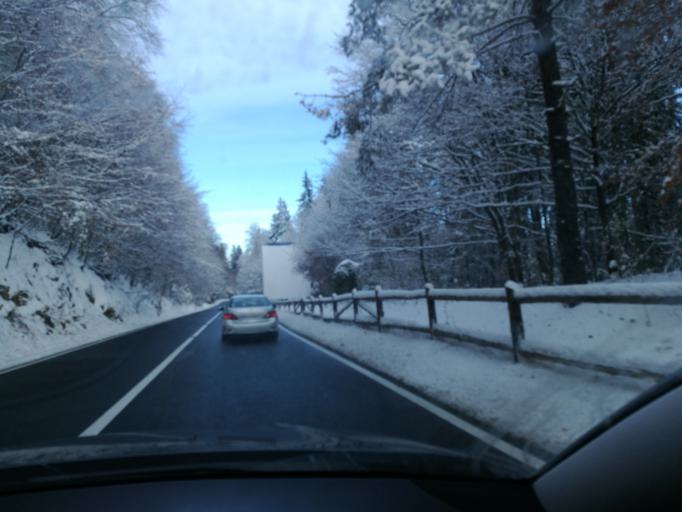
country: RO
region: Brasov
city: Brasov
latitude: 45.6260
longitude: 25.5501
